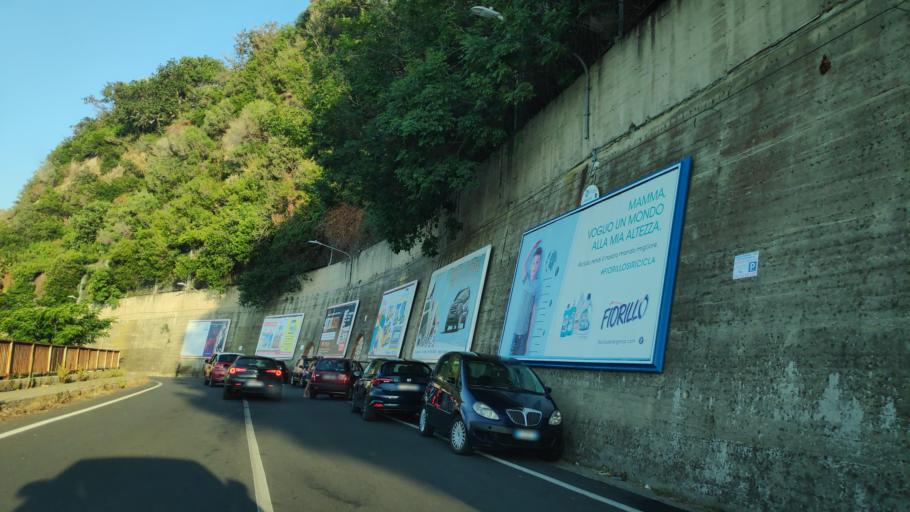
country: IT
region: Calabria
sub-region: Provincia di Reggio Calabria
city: Scilla
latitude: 38.2536
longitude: 15.7194
